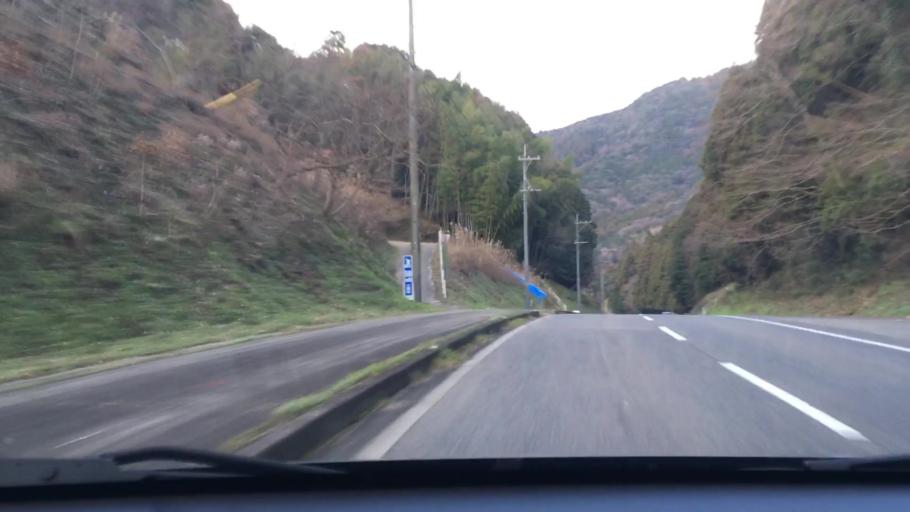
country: JP
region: Oita
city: Bungo-Takada-shi
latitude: 33.4766
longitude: 131.3850
